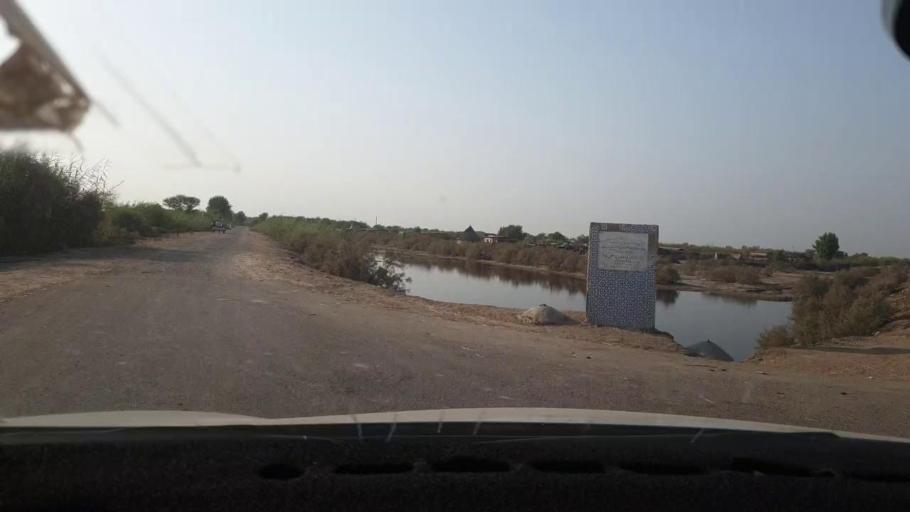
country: PK
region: Sindh
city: Berani
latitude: 25.8151
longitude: 68.8012
